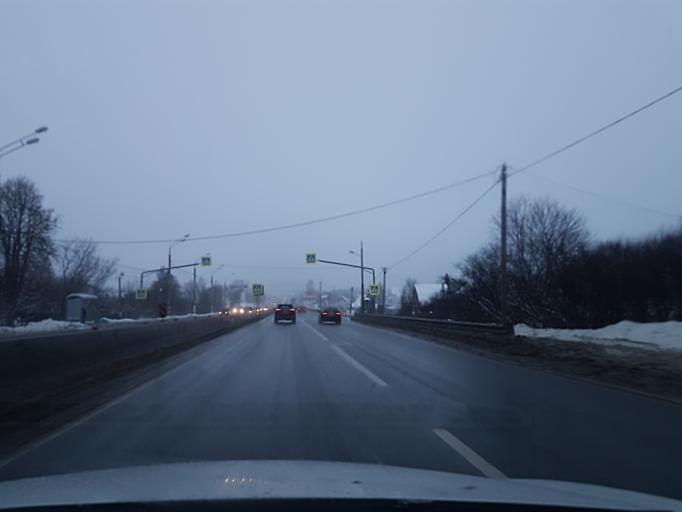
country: RU
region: Moskovskaya
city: Solnechnogorsk
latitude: 56.1647
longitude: 37.0141
